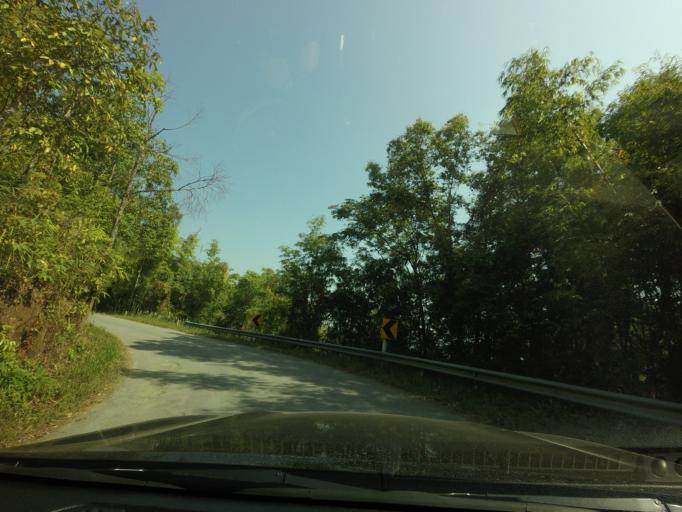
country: TH
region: Kanchanaburi
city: Thong Pha Phum
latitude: 14.6951
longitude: 98.4589
